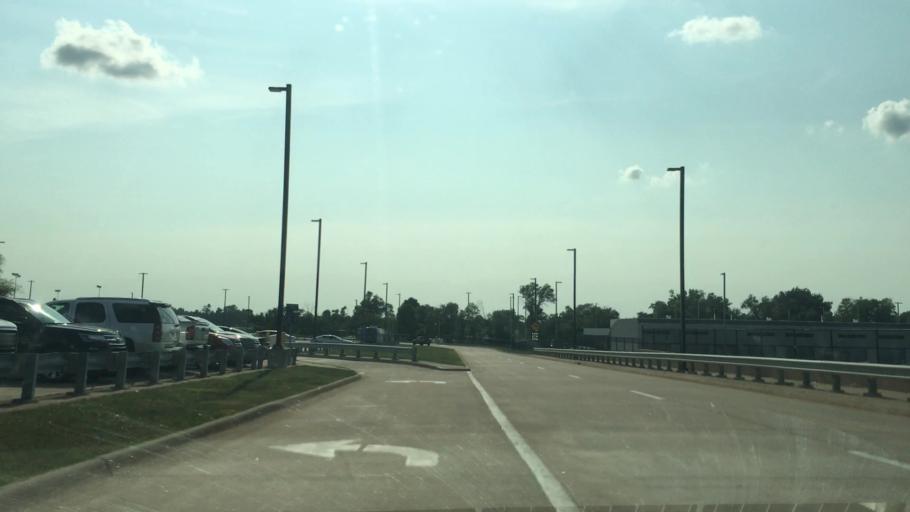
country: US
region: Illinois
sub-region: Rock Island County
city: Moline
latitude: 41.4563
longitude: -90.5059
